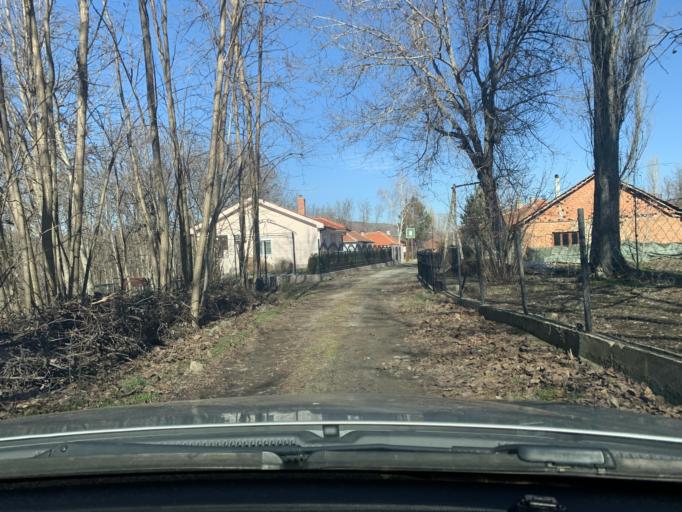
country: MK
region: Demir Kapija
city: Demir Kapija
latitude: 41.3897
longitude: 22.2219
